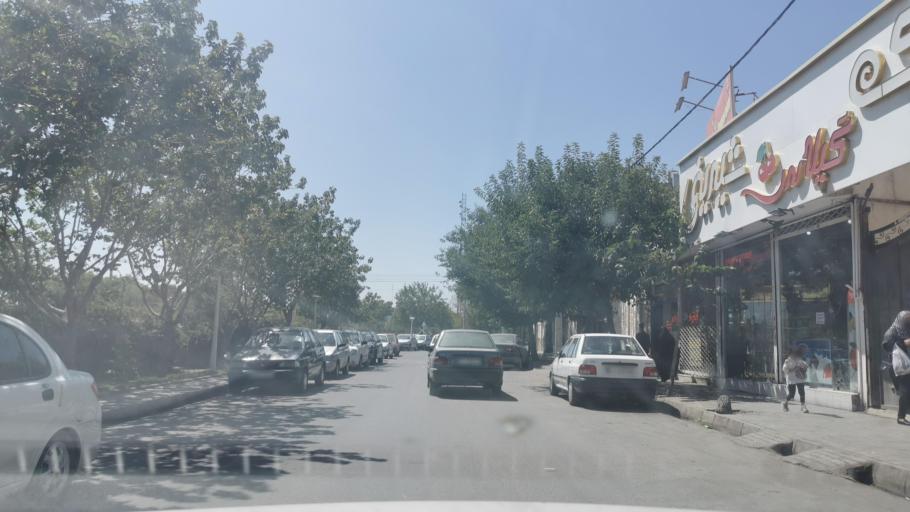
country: IR
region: Razavi Khorasan
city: Mashhad
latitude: 36.3602
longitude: 59.5532
